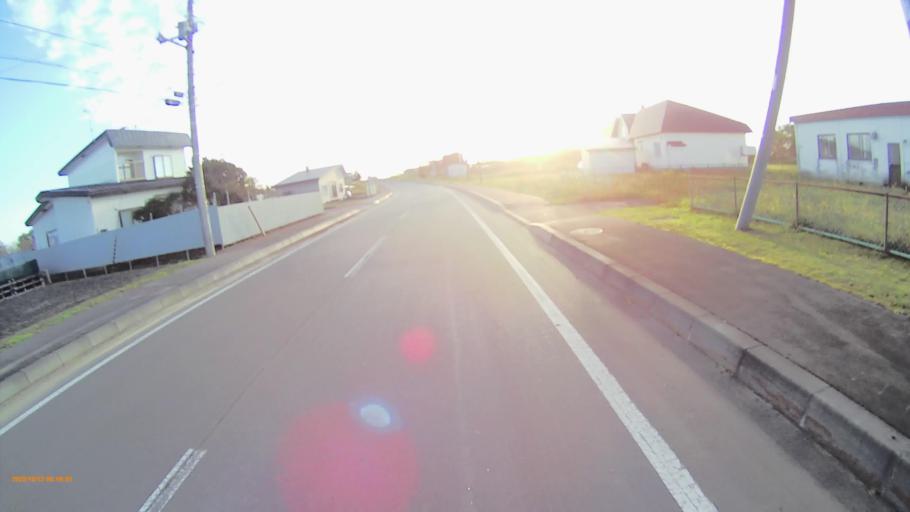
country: JP
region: Hokkaido
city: Kushiro
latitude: 42.8855
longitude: 143.9292
